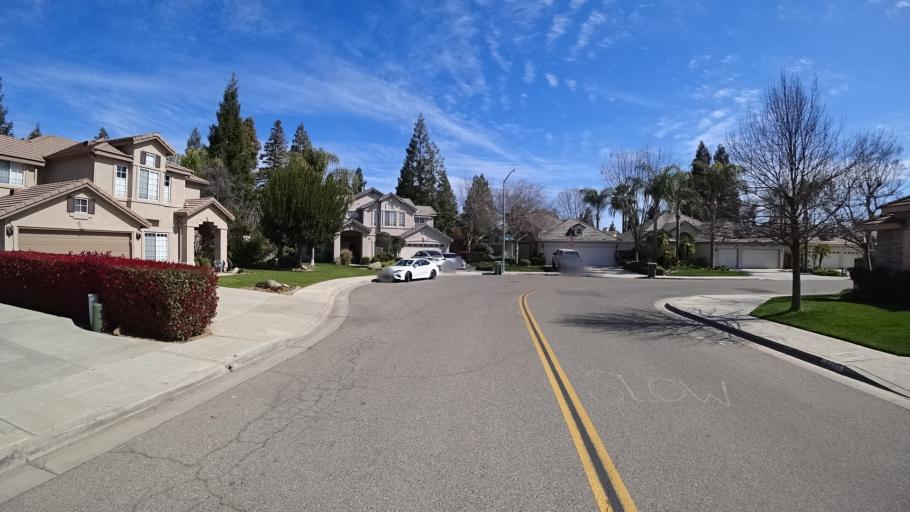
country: US
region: California
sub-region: Fresno County
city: Clovis
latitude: 36.8552
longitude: -119.7688
